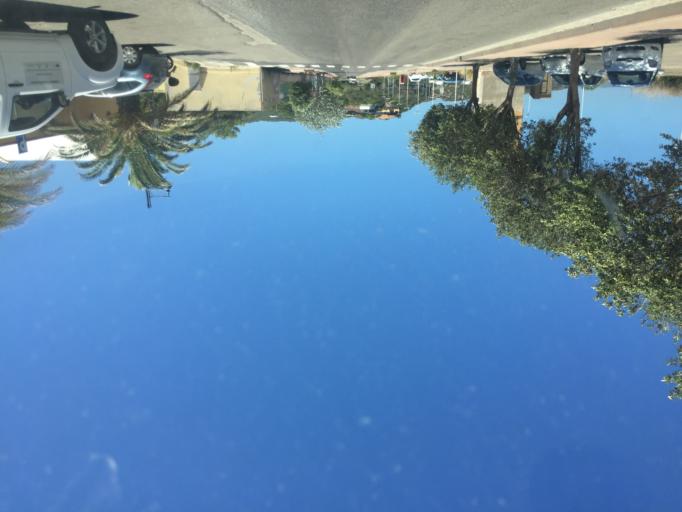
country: IT
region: Sardinia
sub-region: Provincia di Sassari
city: Castelsardo
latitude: 40.9114
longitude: 8.7194
